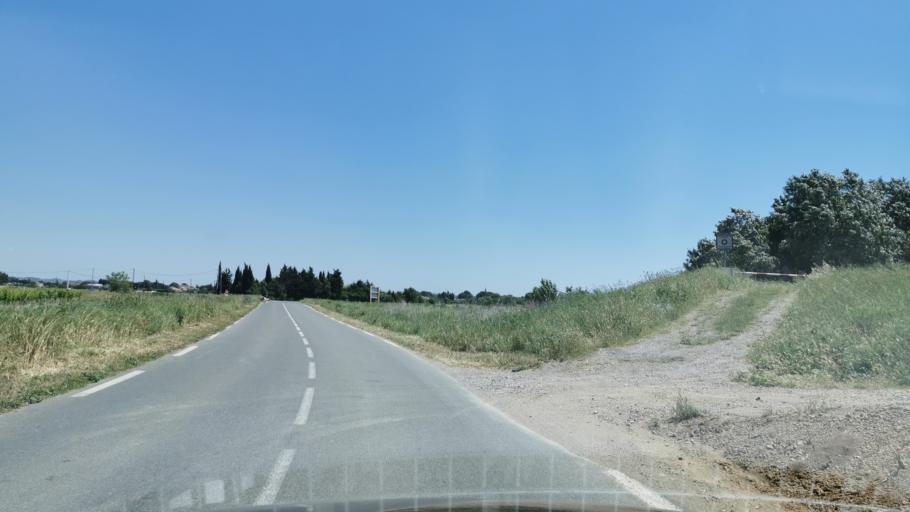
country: FR
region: Languedoc-Roussillon
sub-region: Departement de l'Aude
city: Moussan
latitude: 43.2473
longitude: 2.9821
